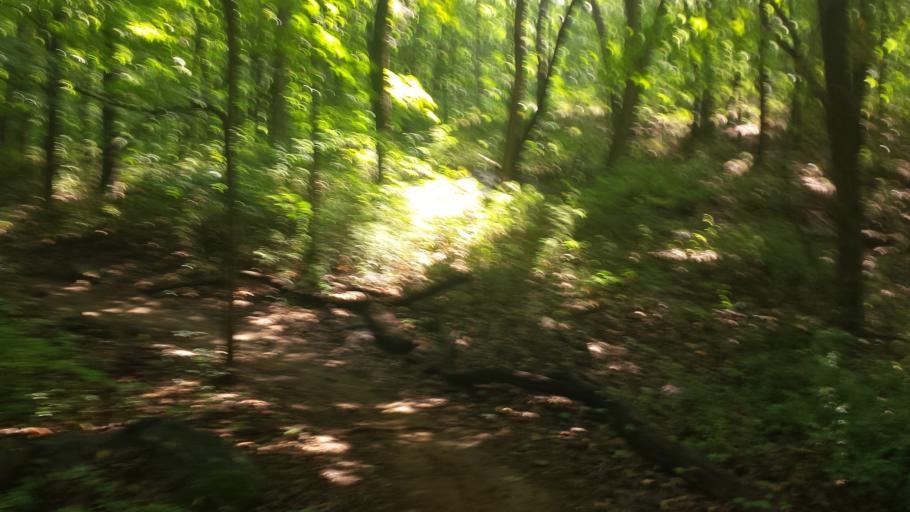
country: US
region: New York
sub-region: Westchester County
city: Hawthorne
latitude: 41.1212
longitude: -73.8041
